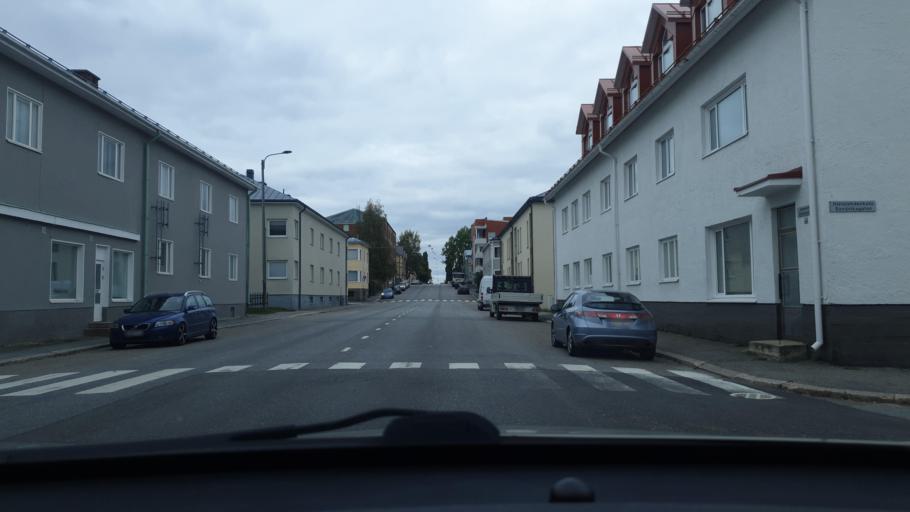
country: FI
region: Ostrobothnia
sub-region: Vaasa
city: Vaasa
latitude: 63.0886
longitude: 21.6287
